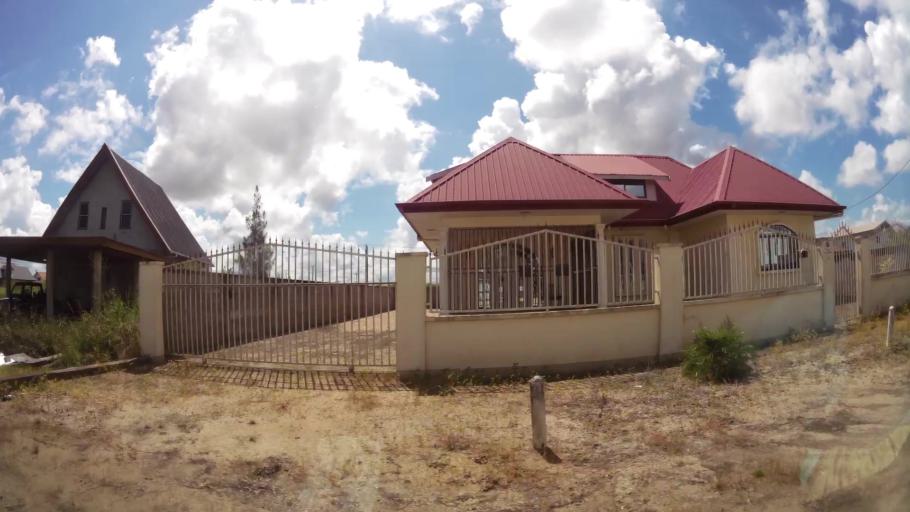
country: SR
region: Paramaribo
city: Paramaribo
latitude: 5.8695
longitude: -55.1334
